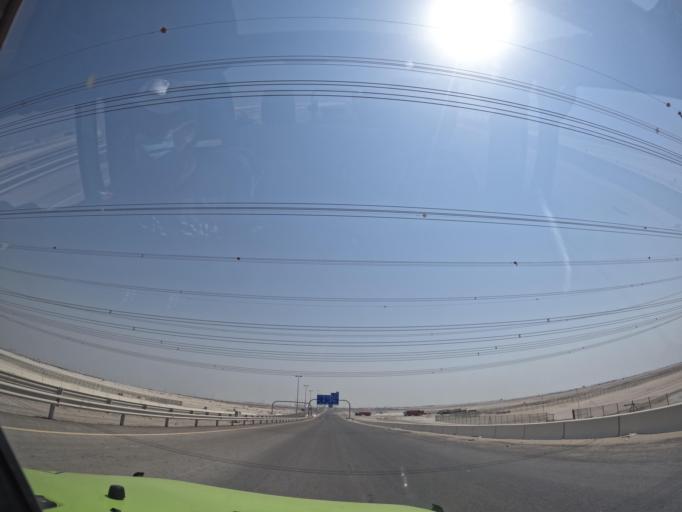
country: AE
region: Abu Dhabi
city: Abu Dhabi
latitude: 24.2544
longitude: 54.4649
